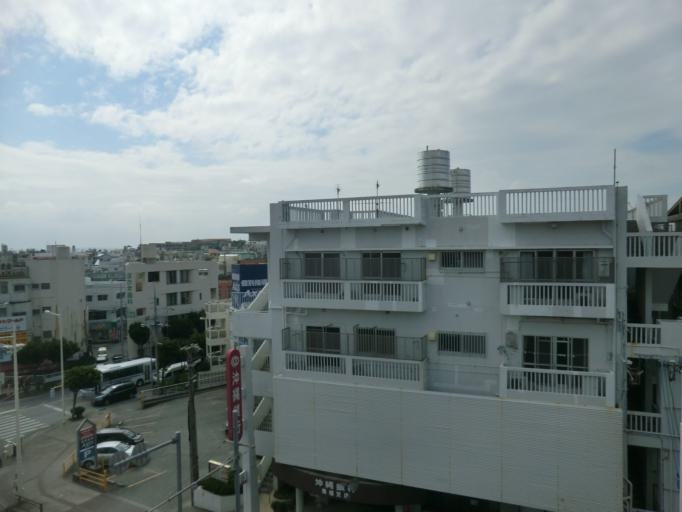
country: JP
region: Okinawa
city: Naha-shi
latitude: 26.2188
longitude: 127.7238
